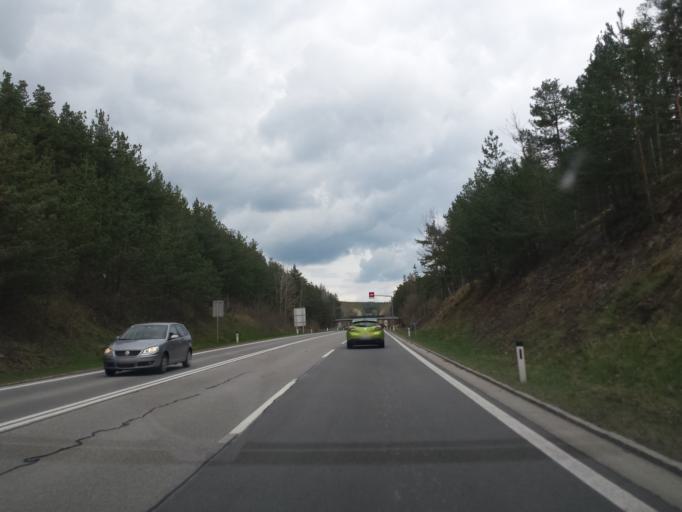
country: AT
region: Lower Austria
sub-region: Politischer Bezirk Krems
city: Lengenfeld
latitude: 48.4753
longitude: 15.5795
